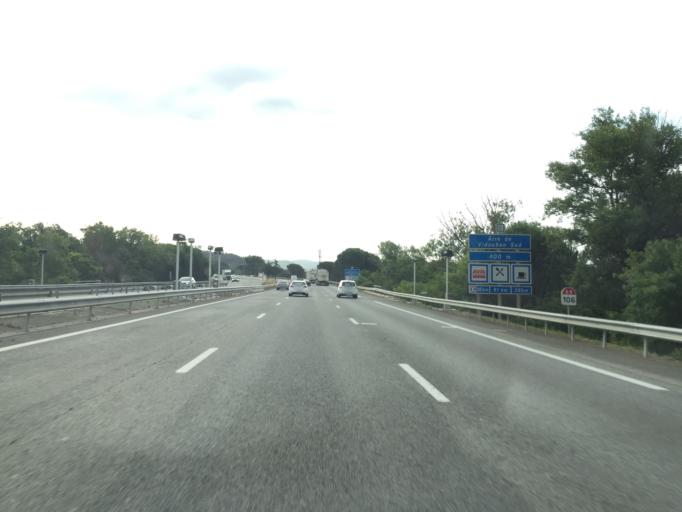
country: FR
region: Provence-Alpes-Cote d'Azur
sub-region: Departement du Var
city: Vidauban
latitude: 43.4138
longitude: 6.4430
